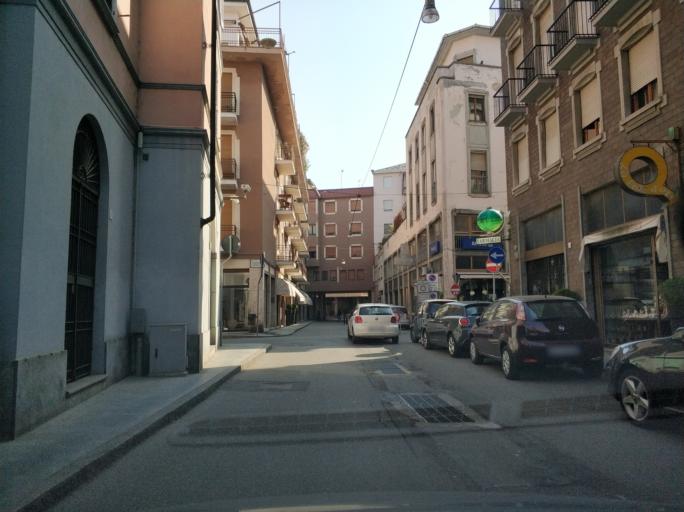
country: IT
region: Piedmont
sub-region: Provincia di Vercelli
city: Vercelli
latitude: 45.3249
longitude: 8.4212
